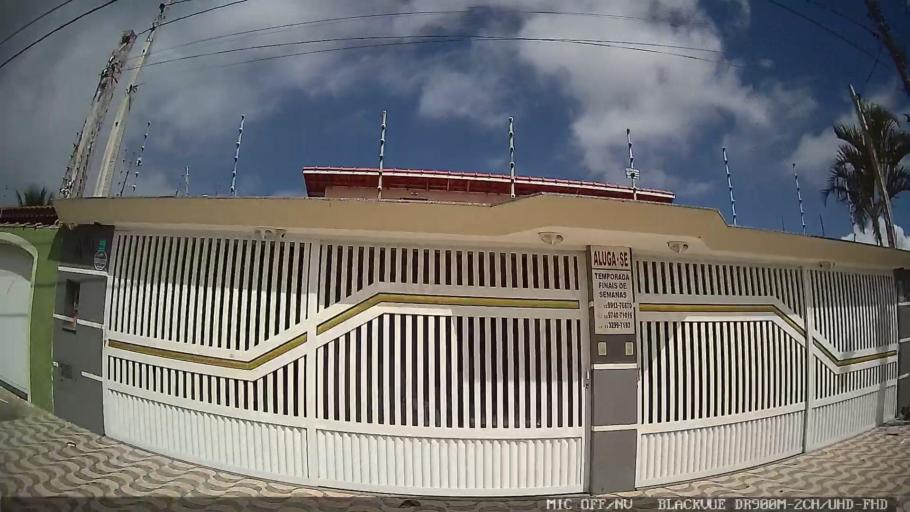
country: BR
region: Sao Paulo
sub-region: Itanhaem
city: Itanhaem
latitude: -24.2275
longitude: -46.8623
